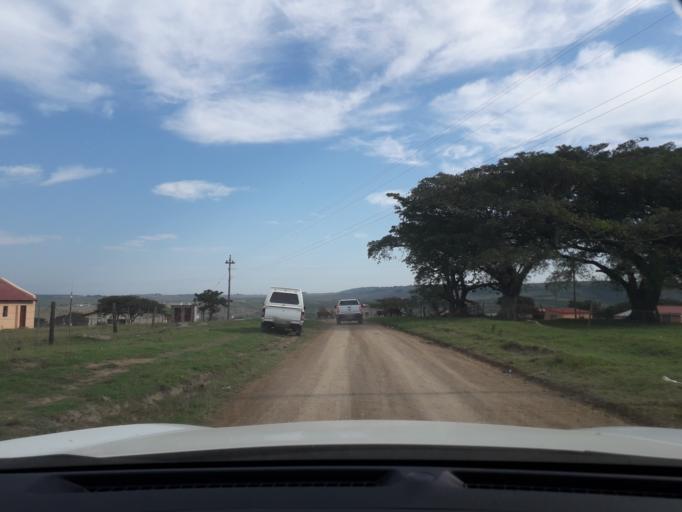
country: ZA
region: Eastern Cape
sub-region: Buffalo City Metropolitan Municipality
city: Bhisho
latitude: -32.9925
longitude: 27.3564
